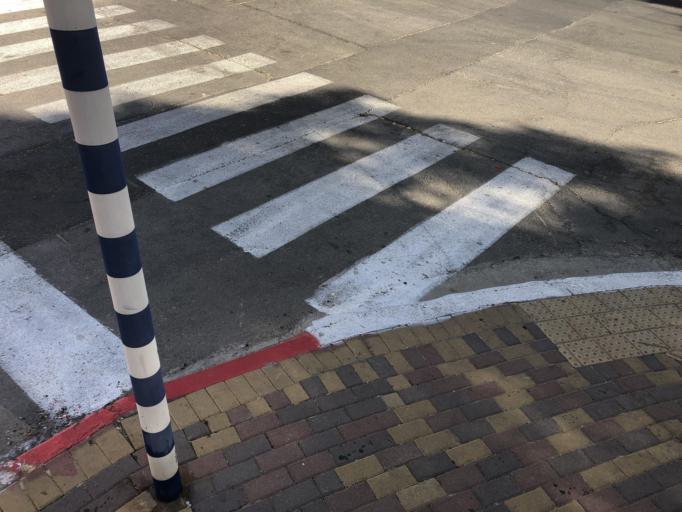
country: IL
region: Central District
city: Yehud
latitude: 32.0341
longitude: 34.8917
